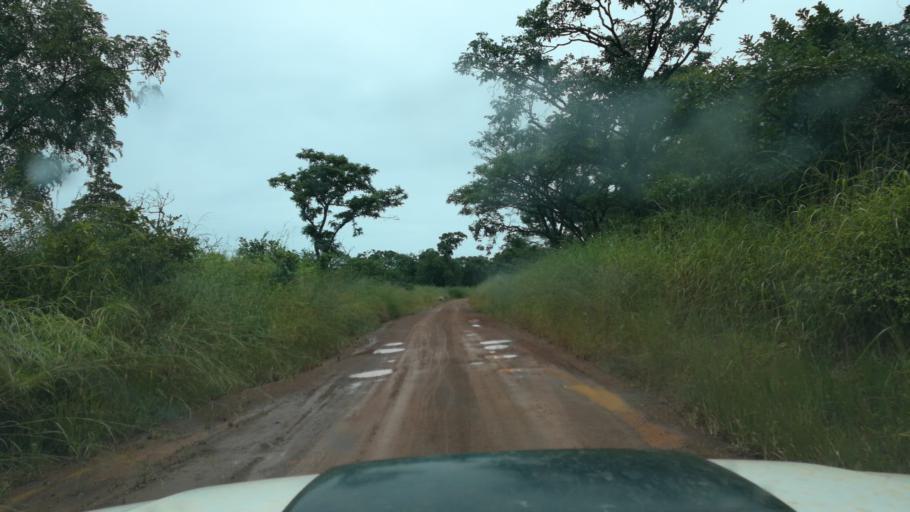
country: ZM
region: Luapula
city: Mwense
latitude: -10.2042
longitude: 28.1037
